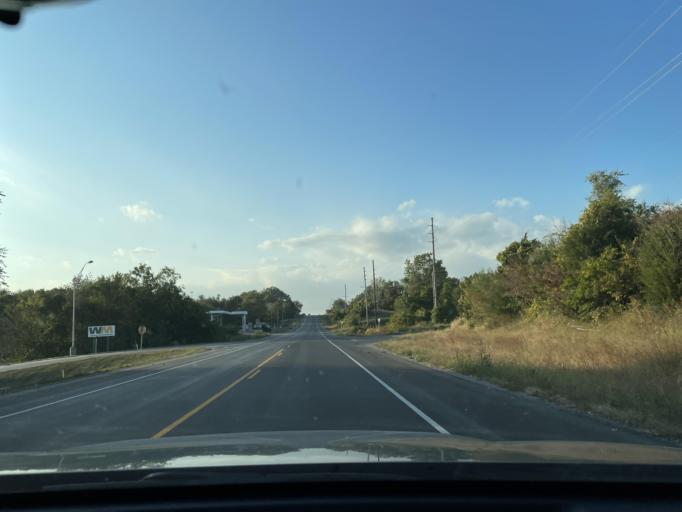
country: US
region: Missouri
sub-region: Andrew County
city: Country Club Village
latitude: 39.8167
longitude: -94.8426
